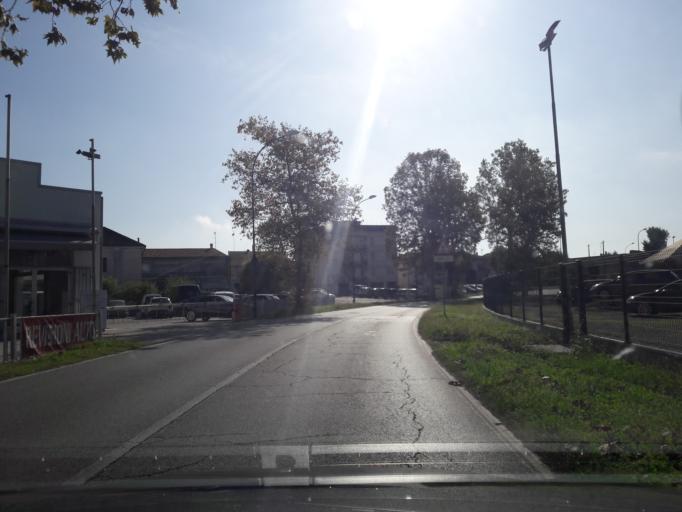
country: IT
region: Veneto
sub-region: Provincia di Venezia
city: Cavarzere
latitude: 45.1339
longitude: 12.0820
